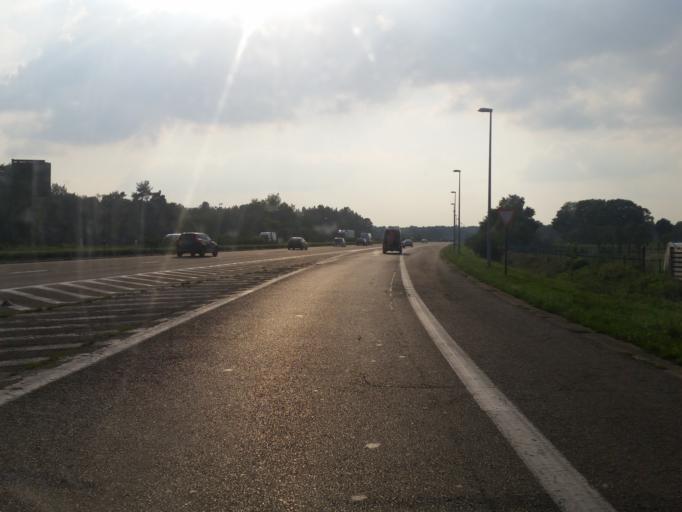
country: BE
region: Flanders
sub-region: Provincie Antwerpen
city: Oud-Turnhout
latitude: 51.2945
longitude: 5.0313
